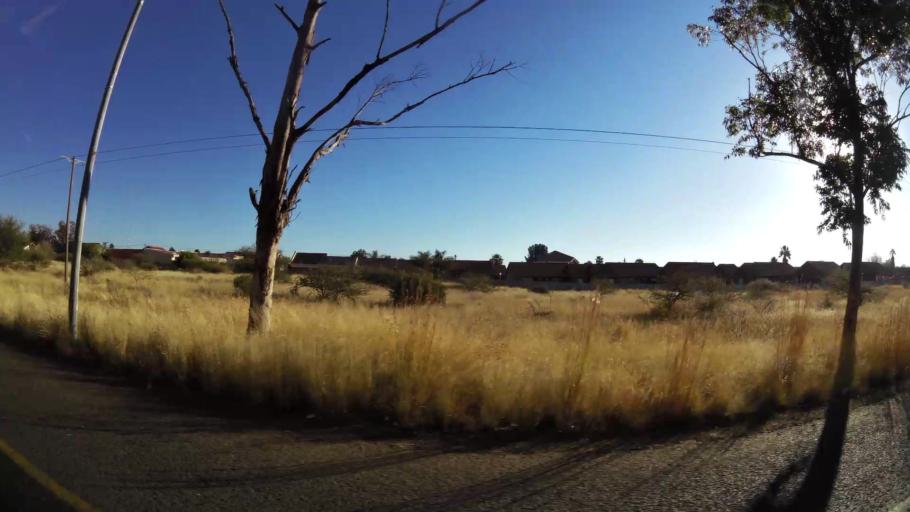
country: ZA
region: Northern Cape
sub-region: Frances Baard District Municipality
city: Kimberley
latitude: -28.7433
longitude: 24.7285
